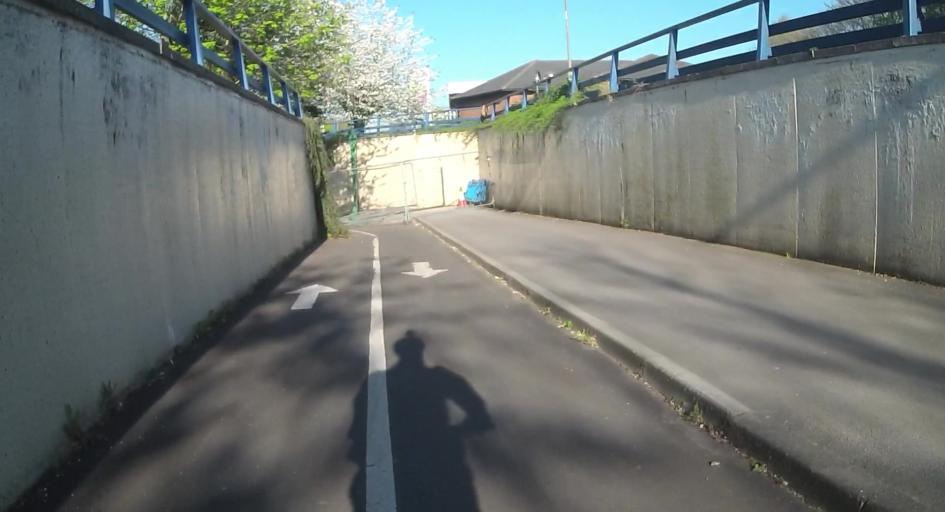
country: GB
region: England
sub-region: Hampshire
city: Basingstoke
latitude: 51.2641
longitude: -1.1164
